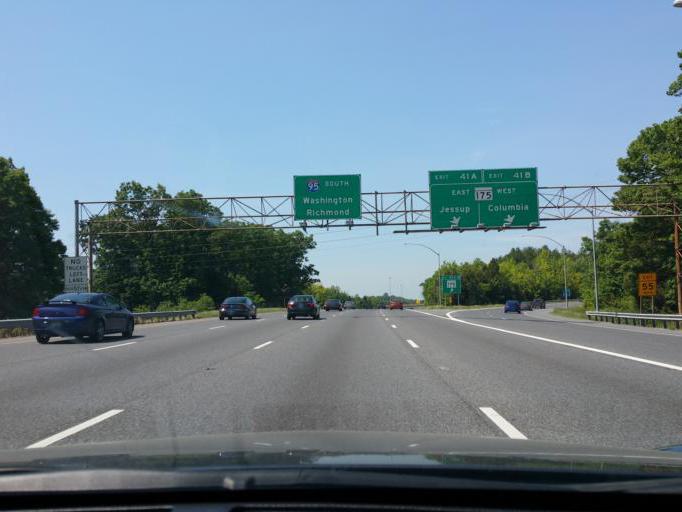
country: US
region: Maryland
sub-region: Anne Arundel County
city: Jessup
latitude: 39.1818
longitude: -76.7842
